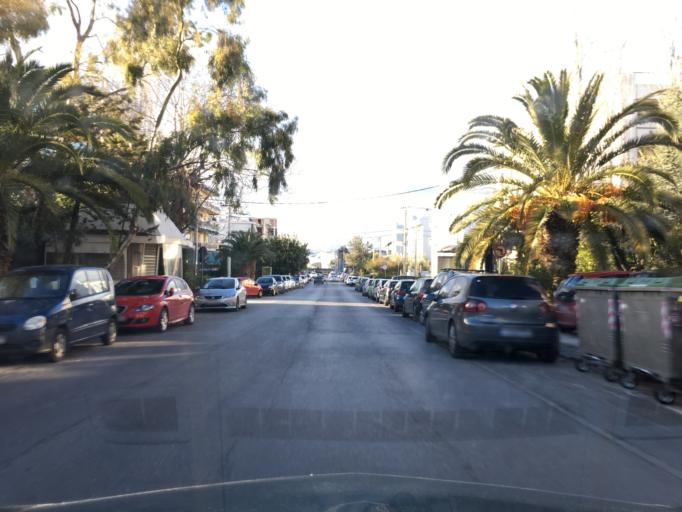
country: GR
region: Attica
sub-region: Nomarchia Athinas
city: Khalandrion
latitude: 38.0303
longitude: 23.7977
